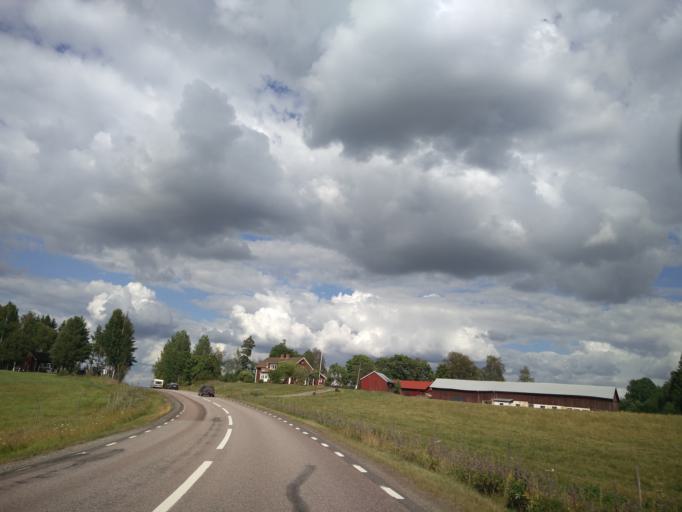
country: SE
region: Vaermland
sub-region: Sunne Kommun
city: Sunne
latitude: 59.7180
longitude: 13.1100
